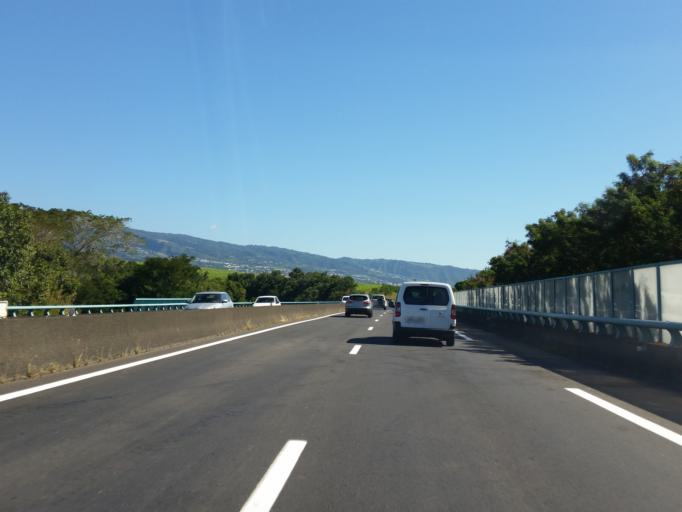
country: RE
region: Reunion
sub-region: Reunion
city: Sainte-Marie
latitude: -20.9027
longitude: 55.5535
